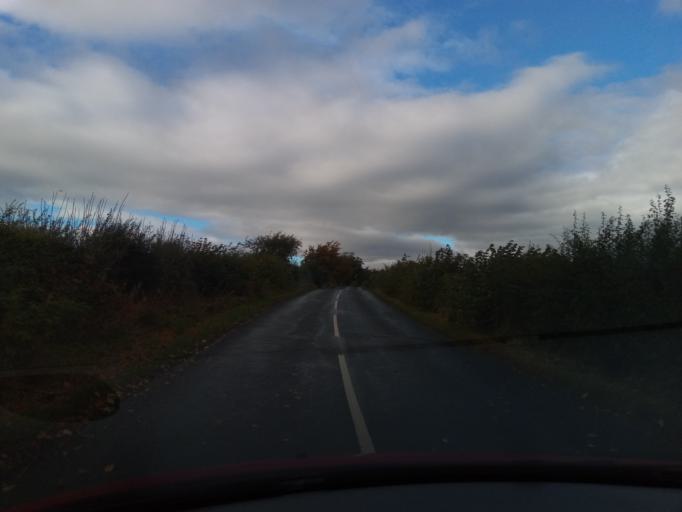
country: GB
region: Scotland
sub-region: The Scottish Borders
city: Newtown St Boswells
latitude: 55.5546
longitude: -2.7069
